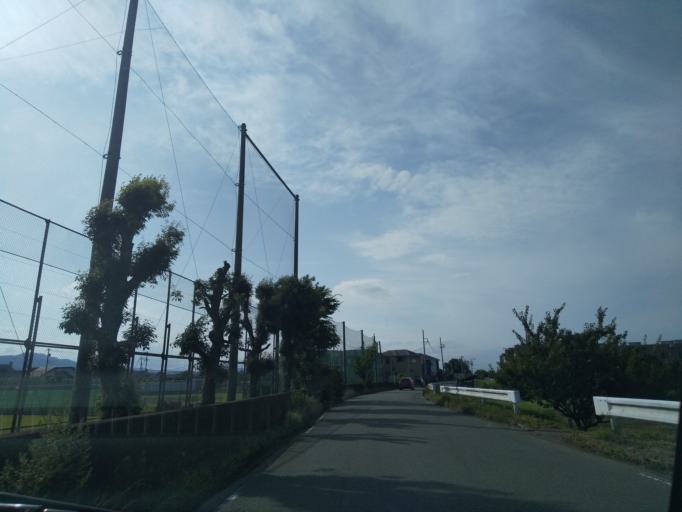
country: JP
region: Kanagawa
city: Zama
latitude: 35.4779
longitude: 139.3808
